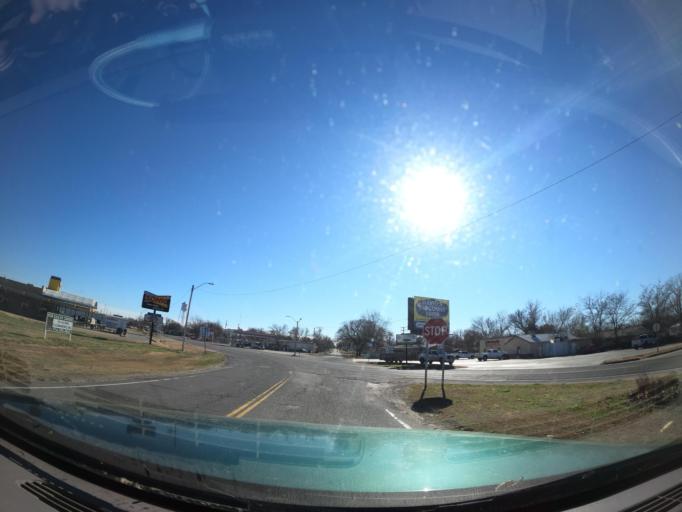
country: US
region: Oklahoma
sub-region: Muskogee County
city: Haskell
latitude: 35.8240
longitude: -95.6775
